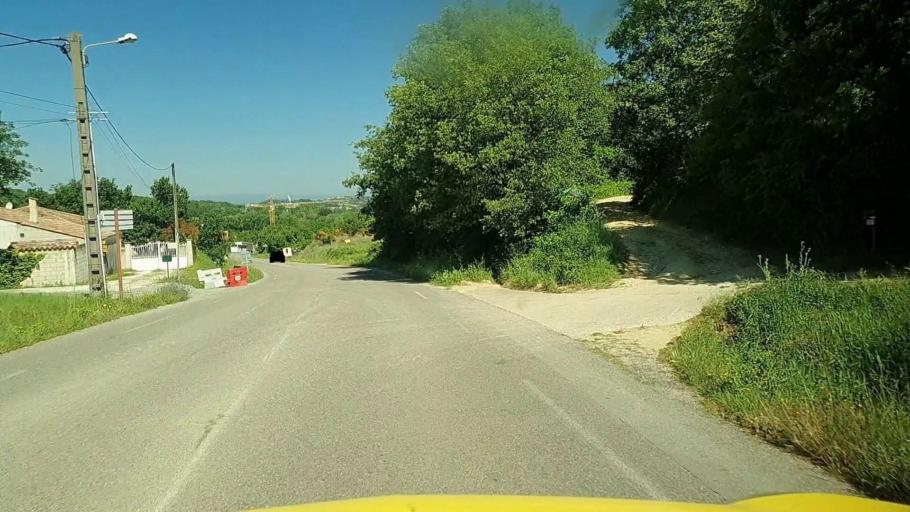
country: FR
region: Languedoc-Roussillon
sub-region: Departement du Gard
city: Moussac
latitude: 43.9864
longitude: 4.2264
